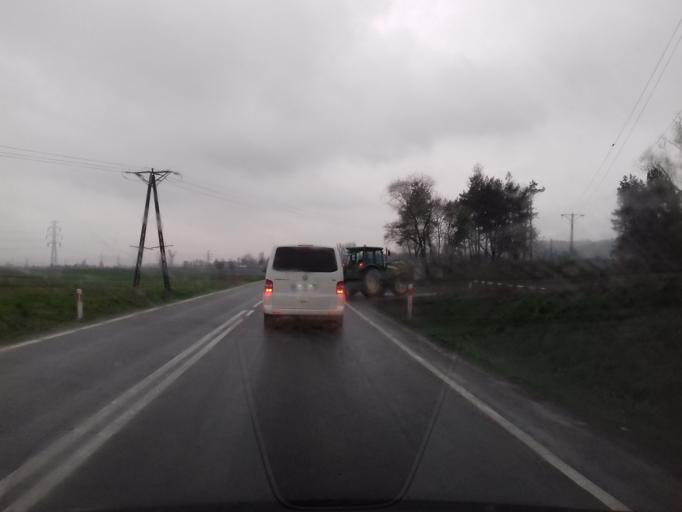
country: PL
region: Lesser Poland Voivodeship
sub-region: Powiat nowosadecki
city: Stary Sacz
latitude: 49.5527
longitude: 20.6548
